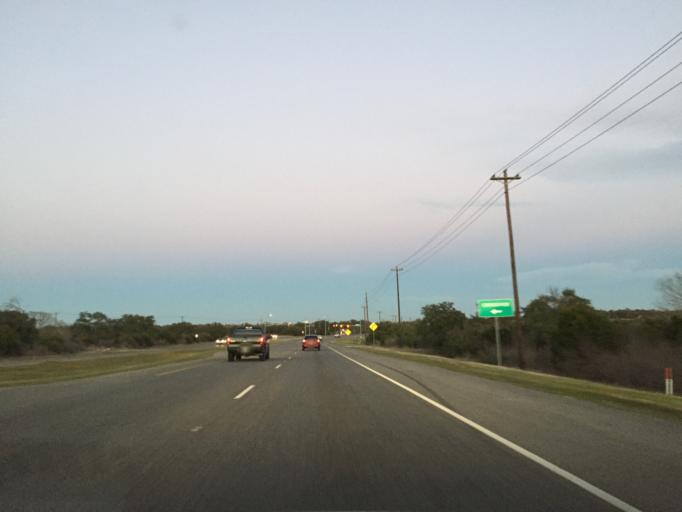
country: US
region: Texas
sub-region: Travis County
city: Jonestown
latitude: 30.5146
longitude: -97.8734
